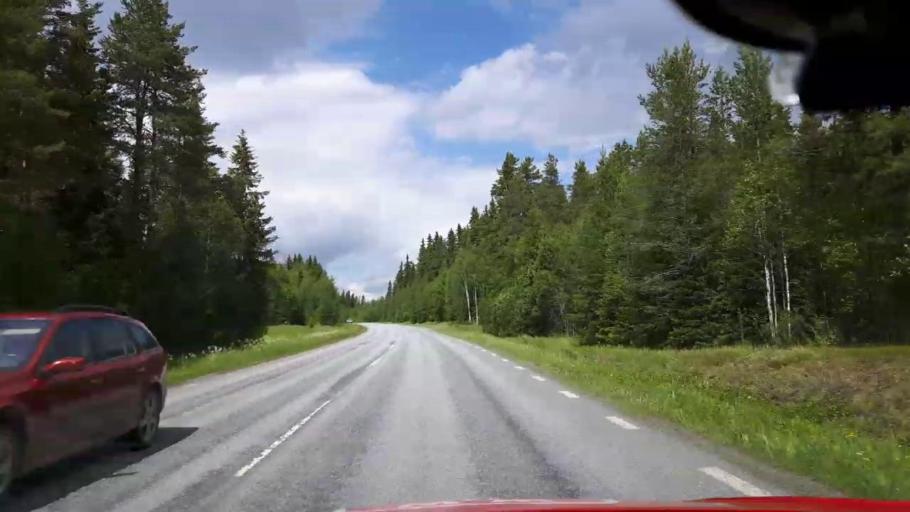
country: SE
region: Jaemtland
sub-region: Krokoms Kommun
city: Krokom
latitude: 63.3767
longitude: 14.3853
